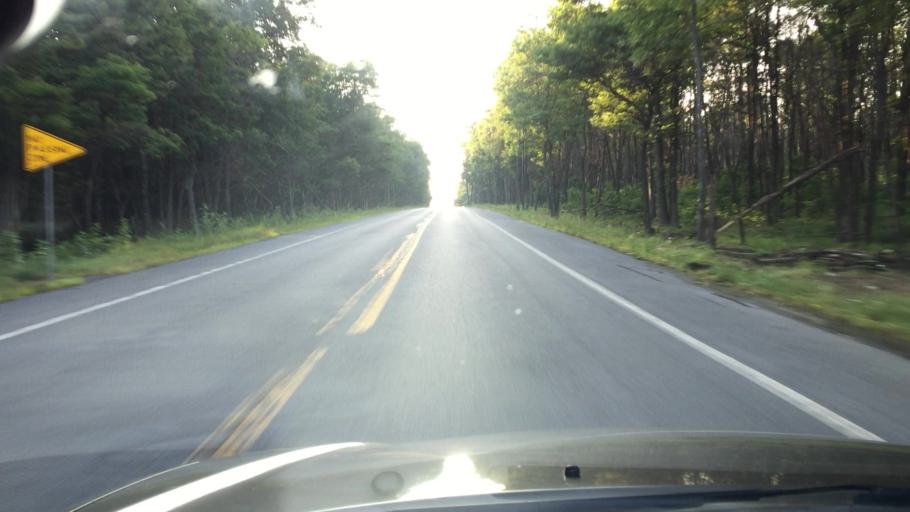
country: US
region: Pennsylvania
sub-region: Carbon County
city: Nesquehoning
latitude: 40.9007
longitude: -75.8175
